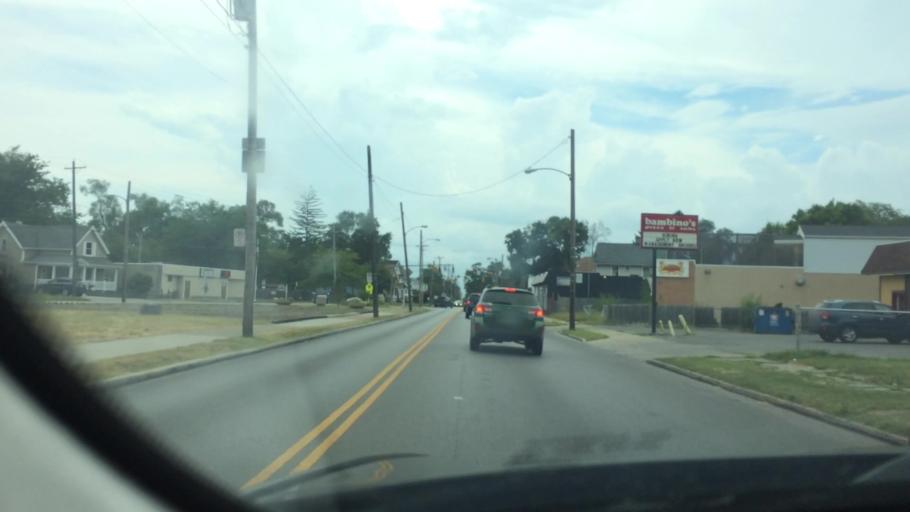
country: US
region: Ohio
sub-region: Wood County
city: Rossford
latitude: 41.6312
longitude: -83.5968
